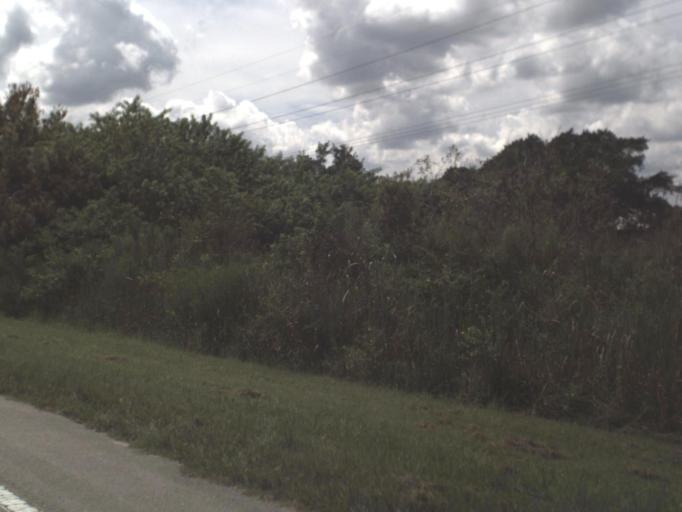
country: US
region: Florida
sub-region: Collier County
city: Orangetree
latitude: 26.0954
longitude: -81.3448
